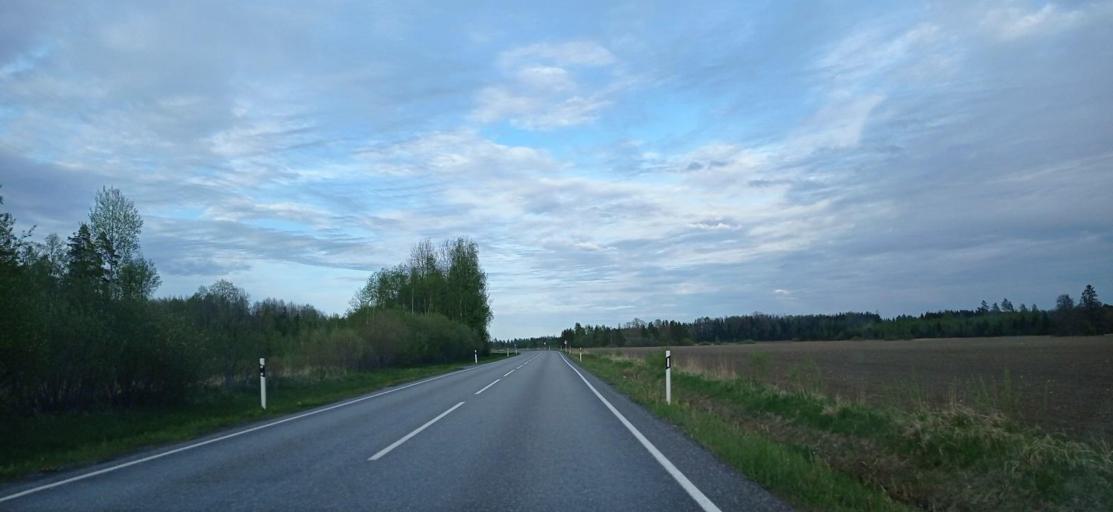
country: EE
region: Paernumaa
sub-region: Sindi linn
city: Sindi
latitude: 58.5227
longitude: 24.6370
